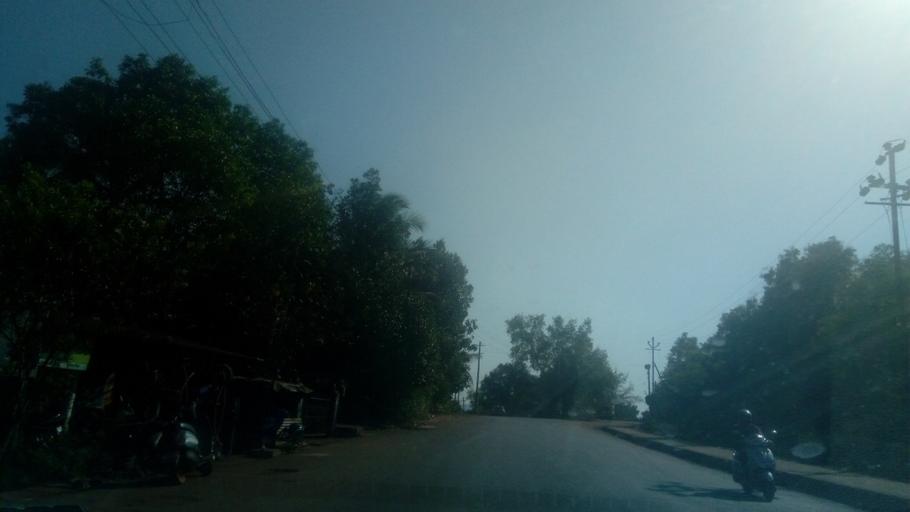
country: IN
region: Goa
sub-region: North Goa
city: Sanquelim
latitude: 15.5549
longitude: 74.0152
